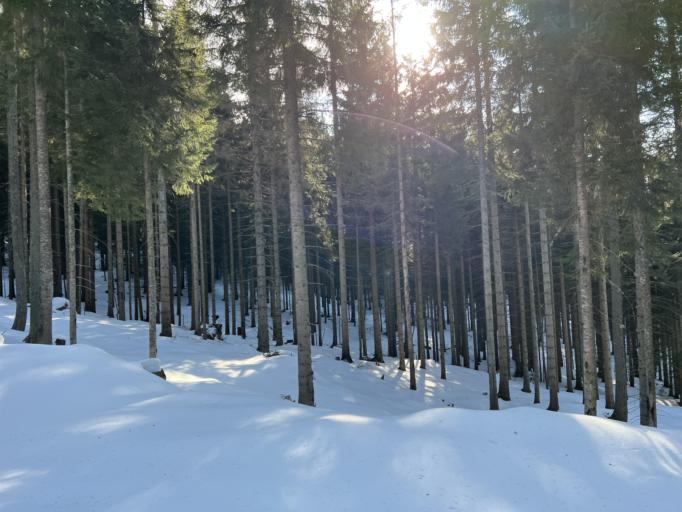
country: AT
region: Carinthia
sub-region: Politischer Bezirk Villach Land
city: Arnoldstein
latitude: 46.5137
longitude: 13.7024
